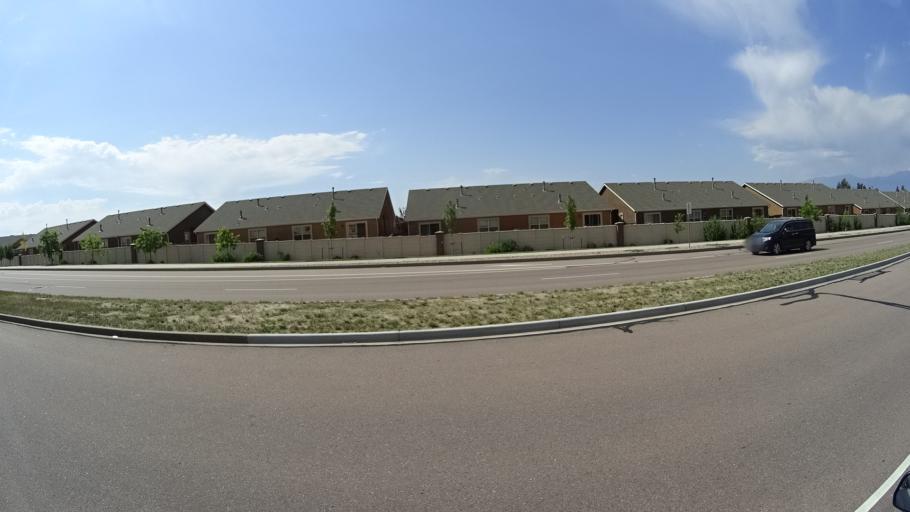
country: US
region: Colorado
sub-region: El Paso County
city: Cimarron Hills
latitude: 38.9295
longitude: -104.7266
